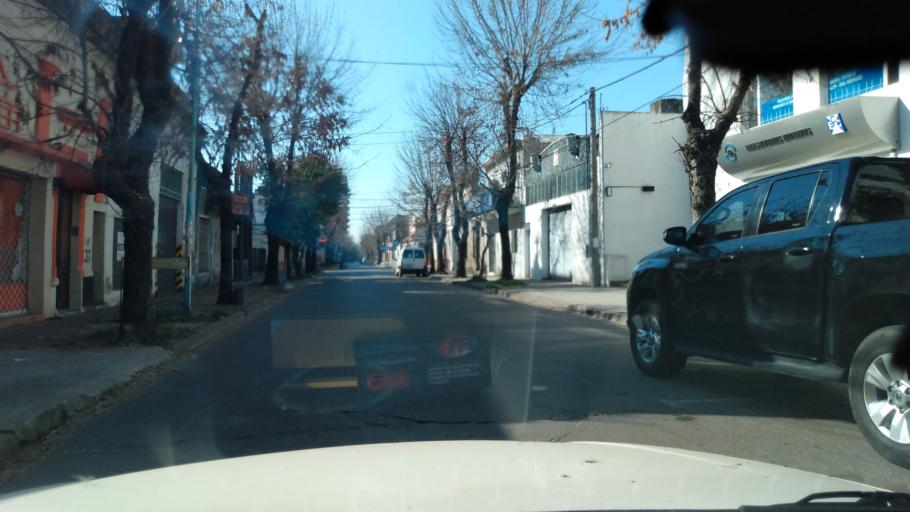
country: AR
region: Buenos Aires
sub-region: Partido de Lujan
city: Lujan
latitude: -34.5683
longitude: -59.1134
